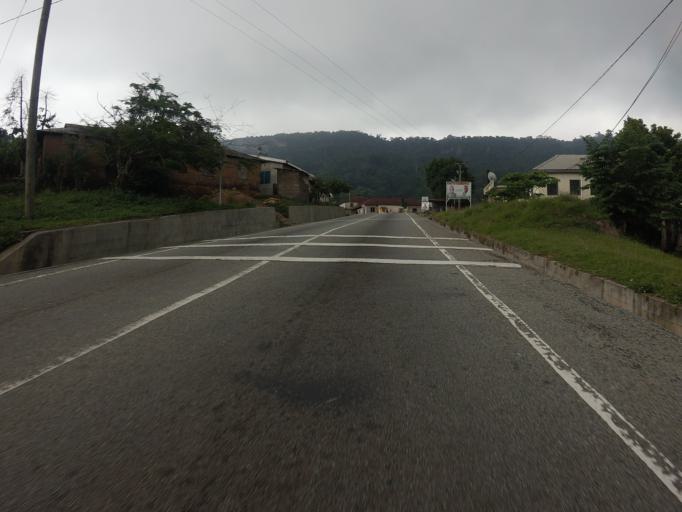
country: GH
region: Volta
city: Kpandu
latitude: 6.8212
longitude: 0.4243
